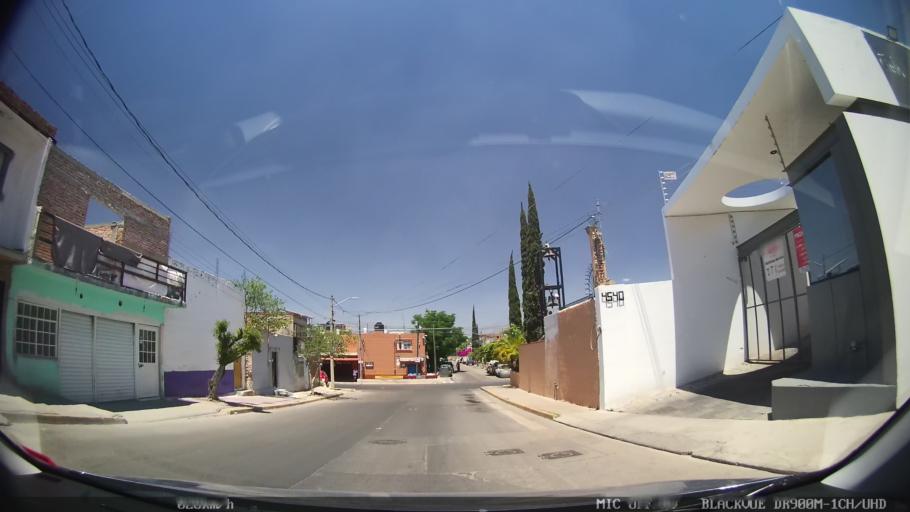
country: MX
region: Jalisco
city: Tlaquepaque
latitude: 20.6476
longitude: -103.2751
